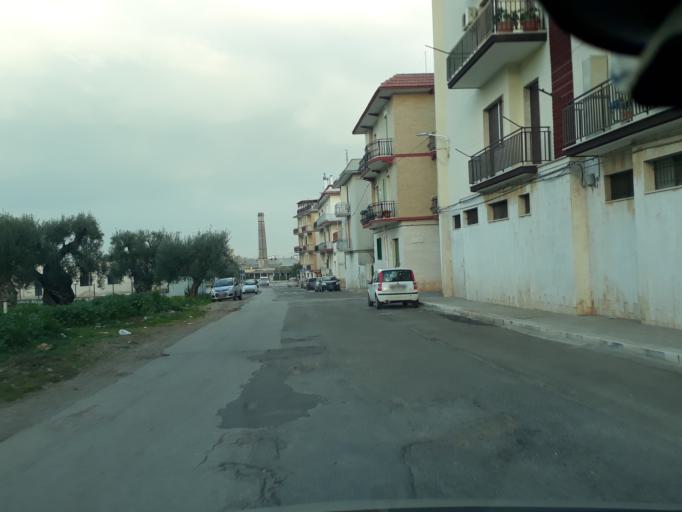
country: IT
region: Apulia
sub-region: Provincia di Brindisi
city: Fasano
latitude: 40.8394
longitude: 17.3553
